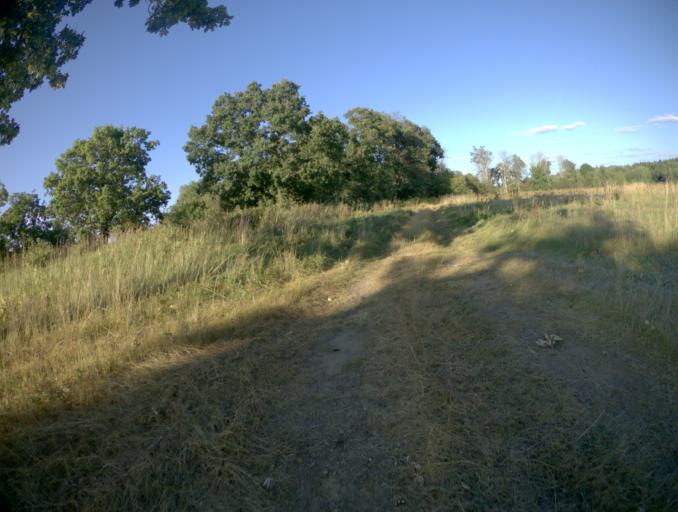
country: RU
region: Vladimir
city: Orgtrud
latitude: 56.1377
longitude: 40.7510
